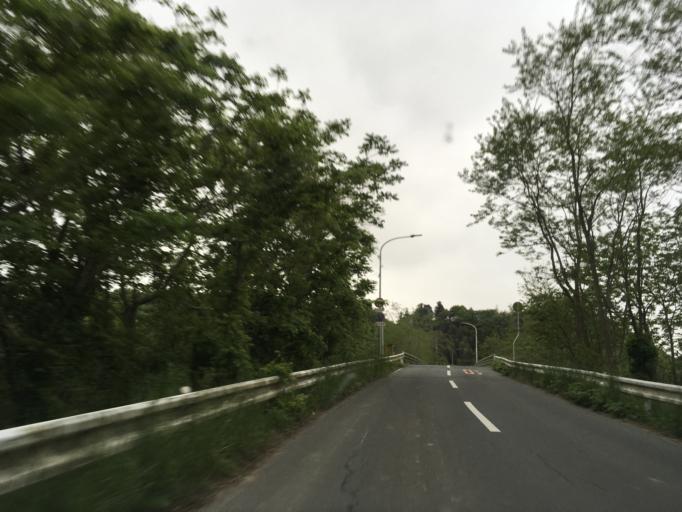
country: JP
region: Miyagi
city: Wakuya
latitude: 38.7155
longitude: 141.2952
